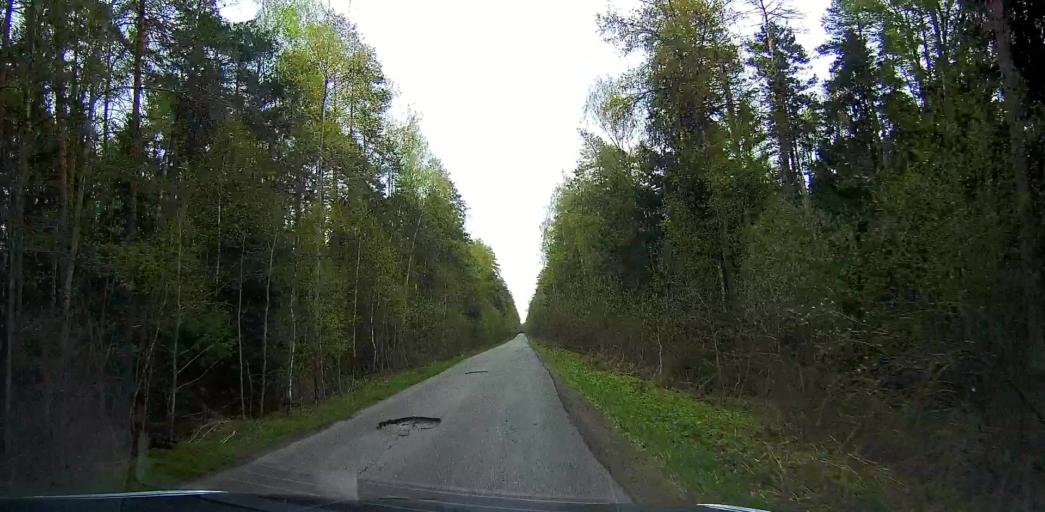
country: RU
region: Moskovskaya
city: Malyshevo
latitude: 55.5479
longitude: 38.3647
